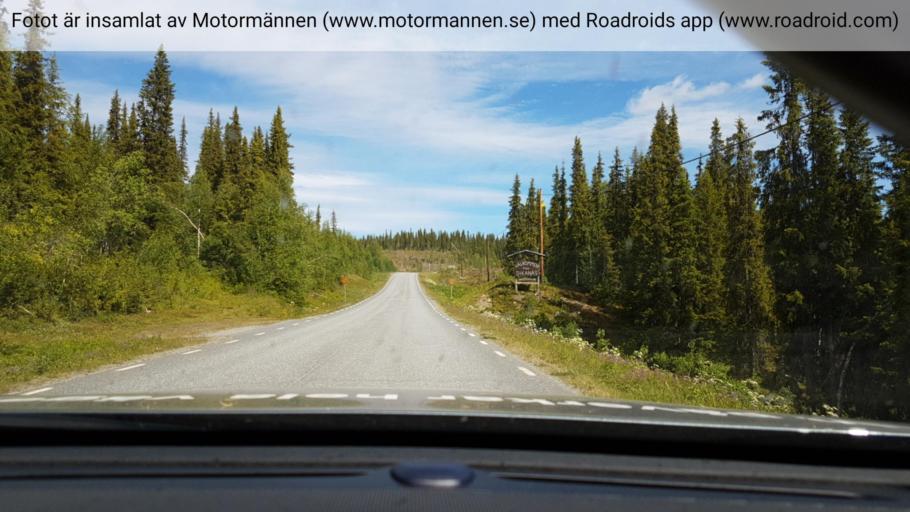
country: SE
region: Vaesterbotten
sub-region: Vilhelmina Kommun
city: Sjoberg
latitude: 65.2304
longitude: 15.9753
